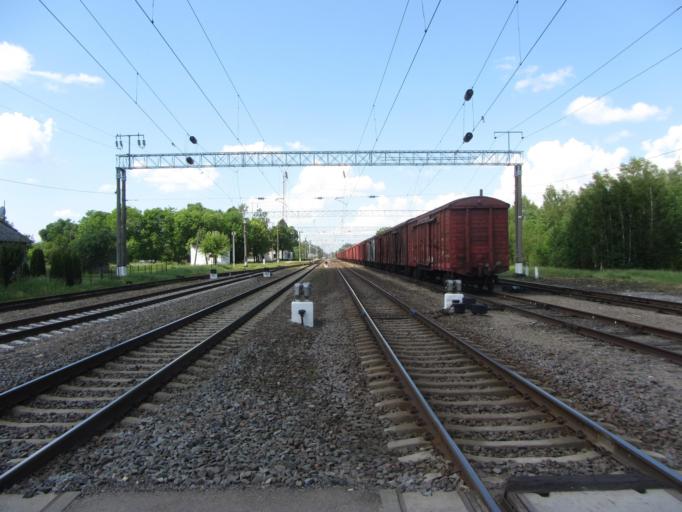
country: LT
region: Kauno apskritis
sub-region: Kauno rajonas
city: Karmelava
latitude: 54.9013
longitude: 24.2246
